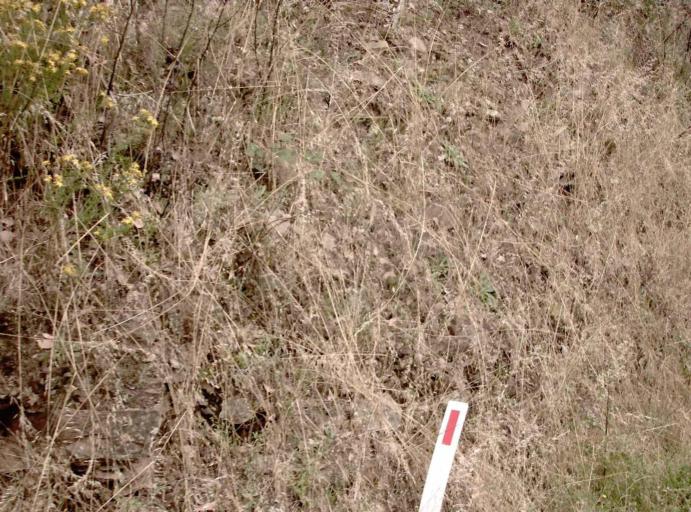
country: AU
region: Victoria
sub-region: Wellington
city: Heyfield
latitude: -37.7836
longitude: 146.6669
